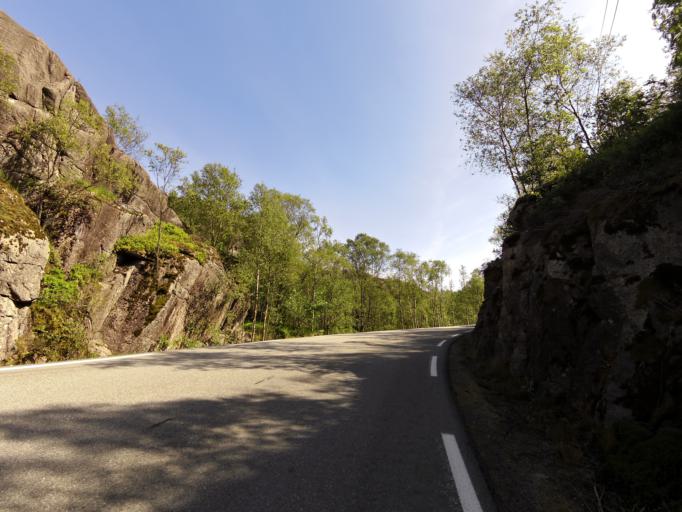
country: NO
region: Rogaland
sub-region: Sokndal
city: Hauge i Dalane
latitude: 58.3407
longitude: 6.3491
